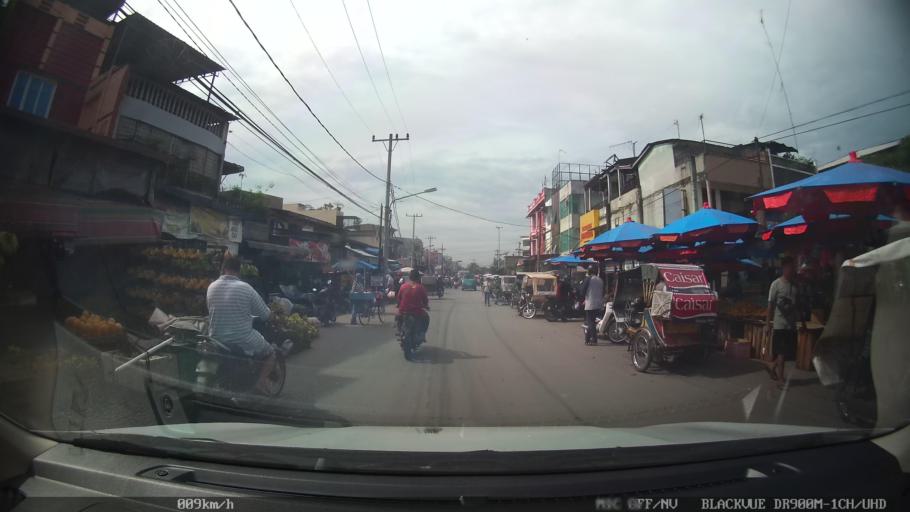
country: ID
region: North Sumatra
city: Sunggal
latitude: 3.5994
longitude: 98.6091
